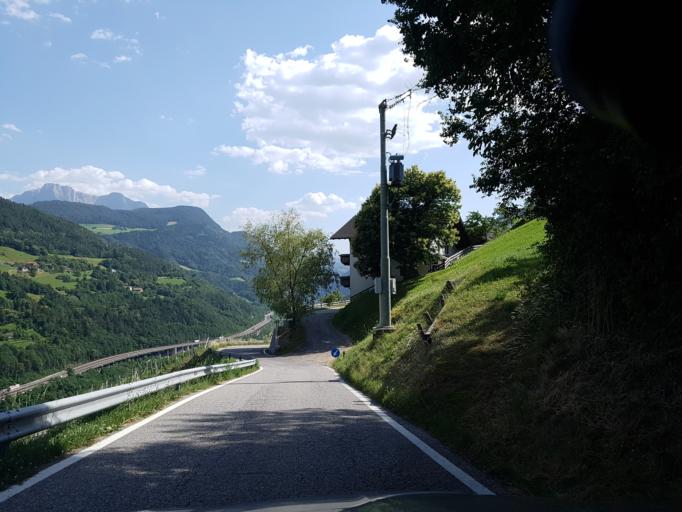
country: IT
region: Trentino-Alto Adige
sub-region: Bolzano
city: Villandro
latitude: 46.6225
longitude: 11.5384
